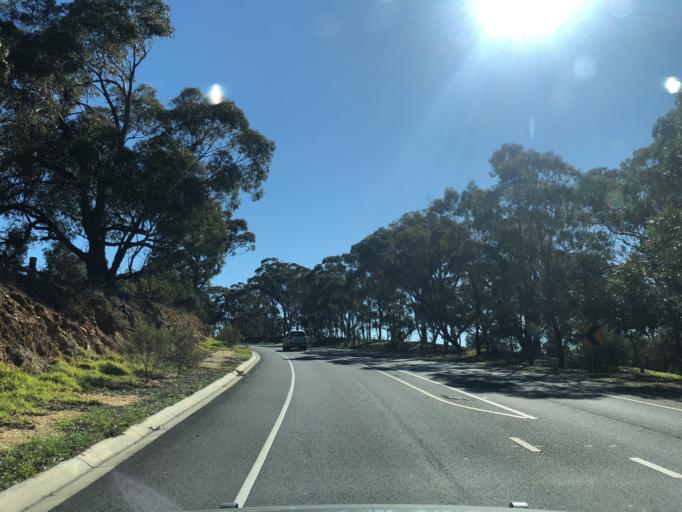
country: AU
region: Victoria
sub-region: Melton
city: Melton West
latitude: -37.6147
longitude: 144.5252
